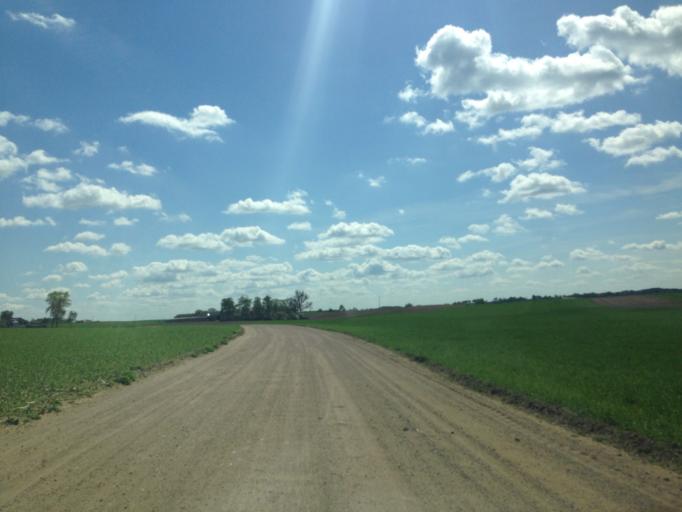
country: PL
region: Kujawsko-Pomorskie
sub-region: Powiat brodnicki
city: Brzozie
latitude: 53.3196
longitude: 19.6150
